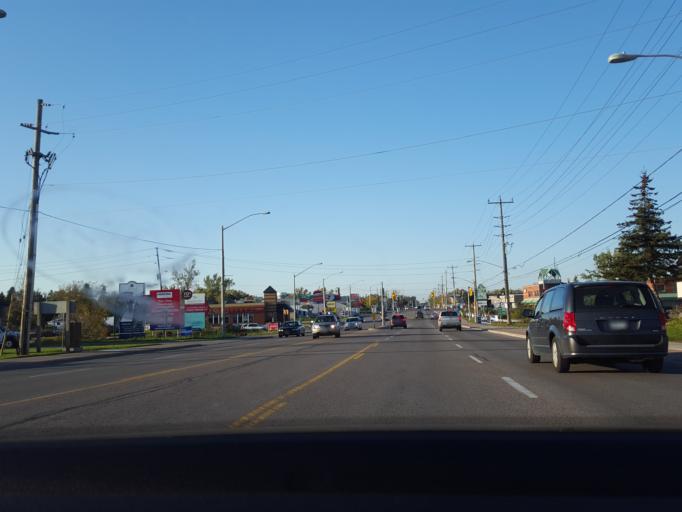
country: CA
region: Ontario
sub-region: York
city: Richmond Hill
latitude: 43.9434
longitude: -79.4543
